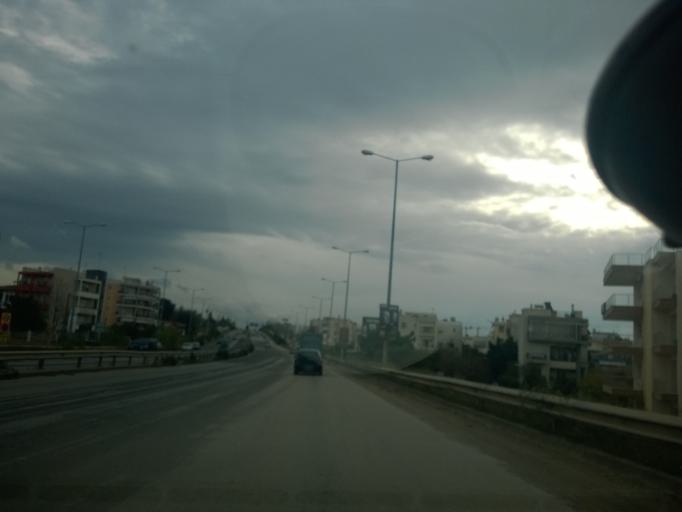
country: GR
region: Central Macedonia
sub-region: Nomos Thessalonikis
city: Kalamaria
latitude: 40.5906
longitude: 22.9667
